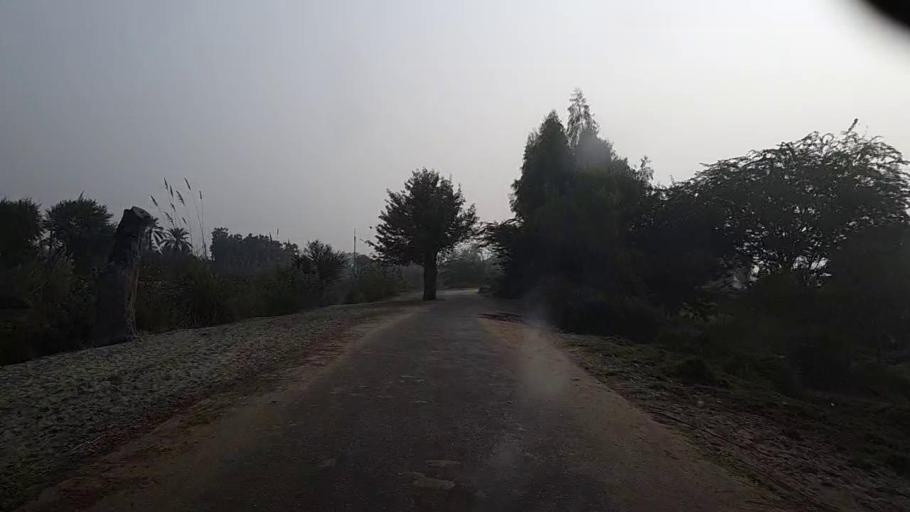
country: PK
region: Sindh
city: Bozdar
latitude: 27.1358
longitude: 68.6536
